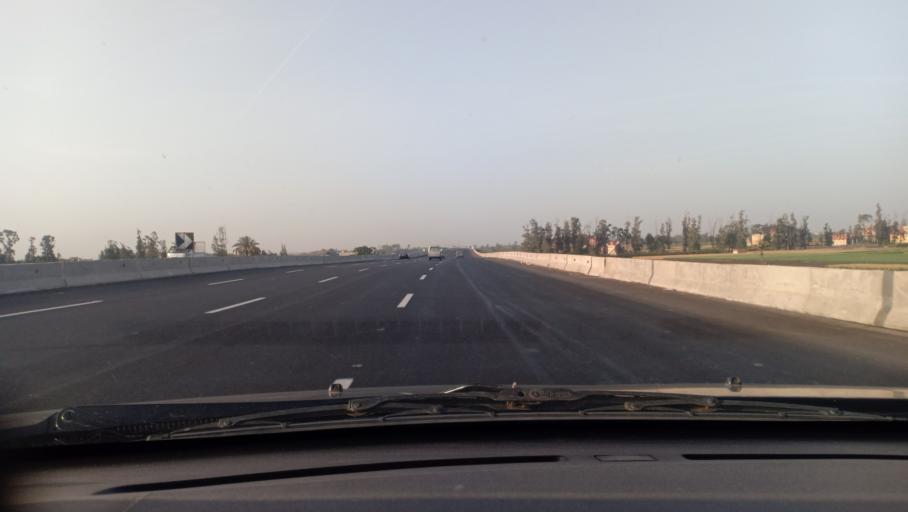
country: EG
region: Muhafazat al Qalyubiyah
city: Toukh
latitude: 30.3066
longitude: 31.2210
